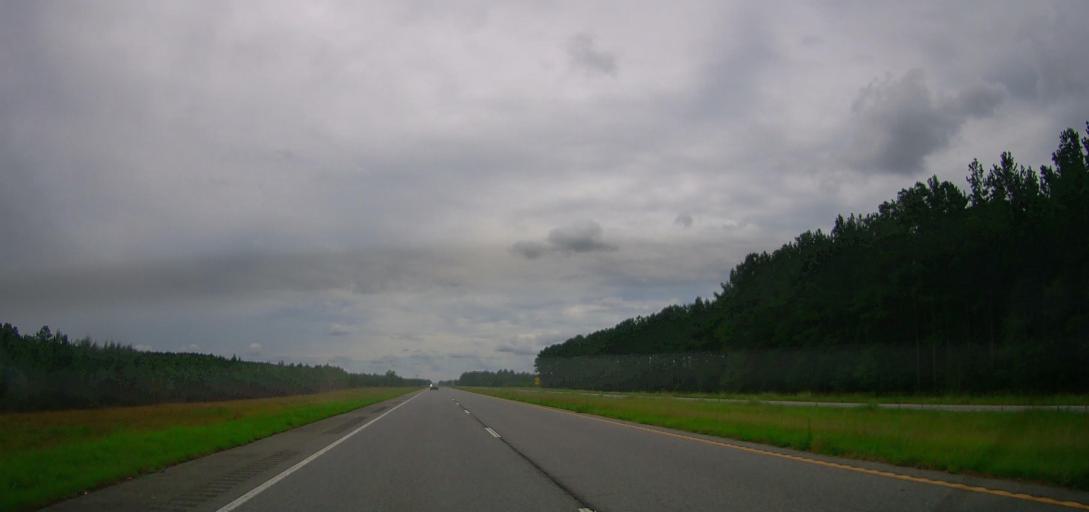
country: US
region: Georgia
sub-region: Appling County
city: Baxley
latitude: 31.7485
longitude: -82.2623
